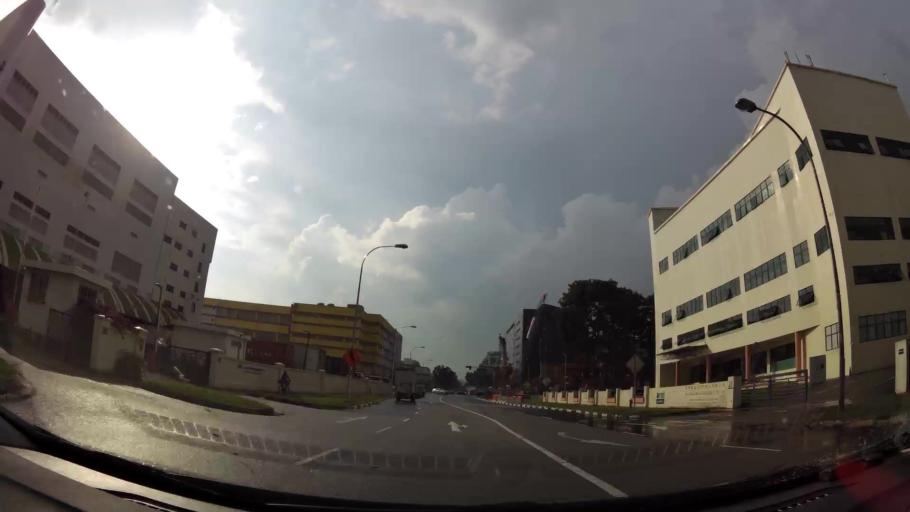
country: SG
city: Singapore
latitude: 1.3314
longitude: 103.9670
